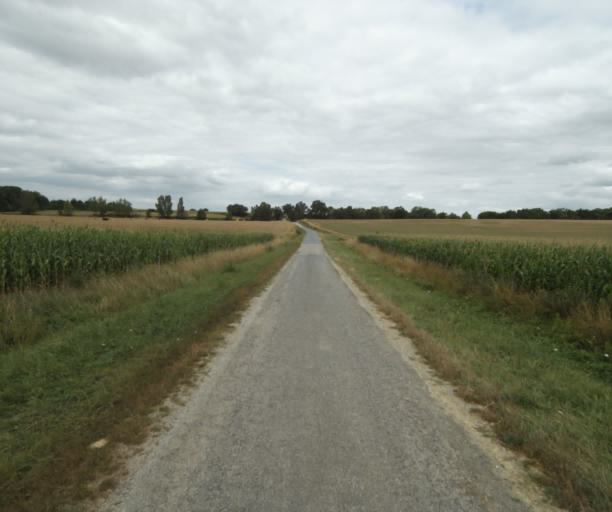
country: FR
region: Midi-Pyrenees
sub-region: Departement du Tarn
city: Soreze
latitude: 43.4642
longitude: 2.0655
